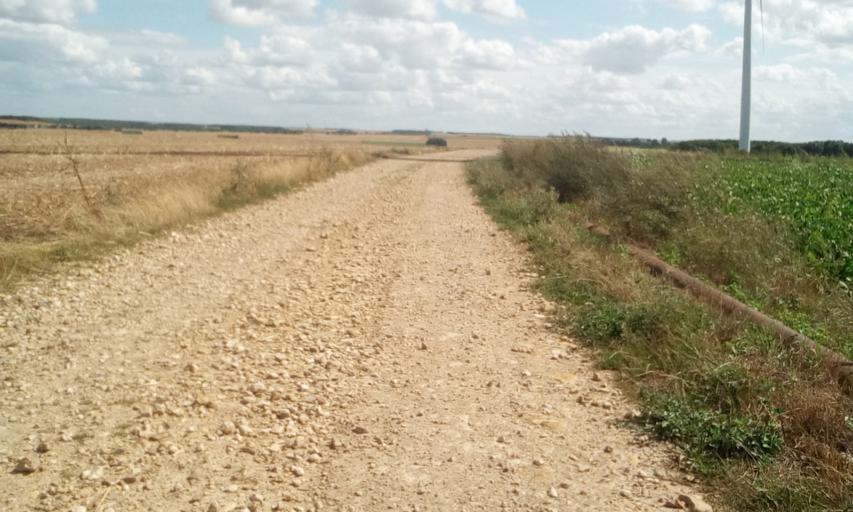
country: FR
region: Lower Normandy
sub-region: Departement du Calvados
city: Bellengreville
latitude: 49.0958
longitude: -0.2253
